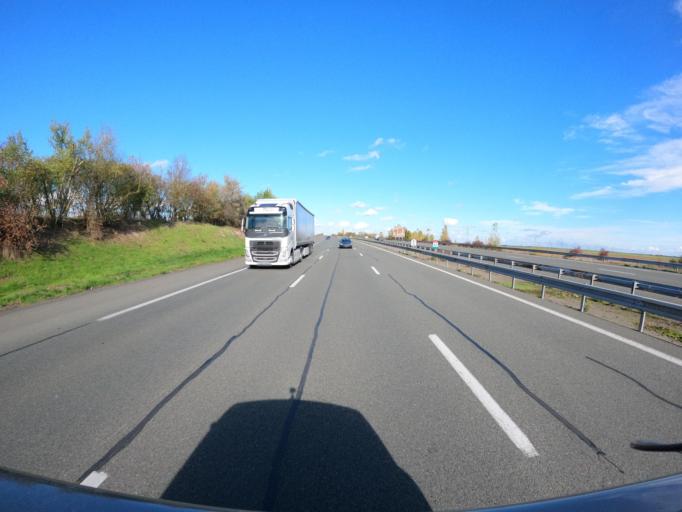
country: FR
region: Centre
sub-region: Departement d'Eure-et-Loir
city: Morancez
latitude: 48.3847
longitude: 1.4905
